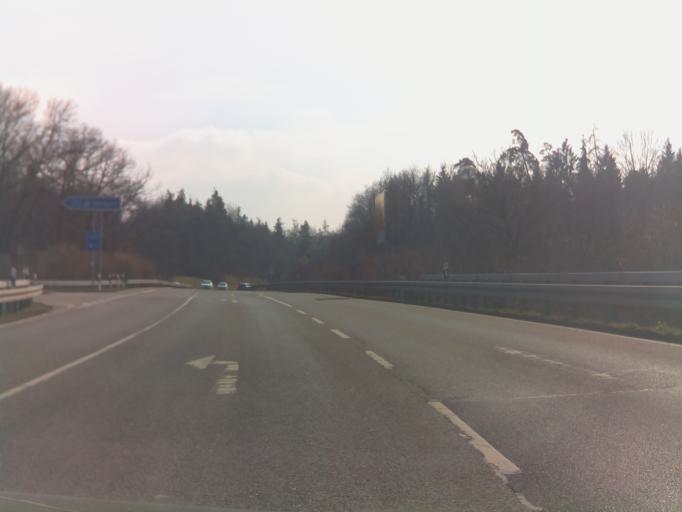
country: DE
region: Baden-Wuerttemberg
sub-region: Regierungsbezirk Stuttgart
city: Ehningen
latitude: 48.6465
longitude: 8.9423
